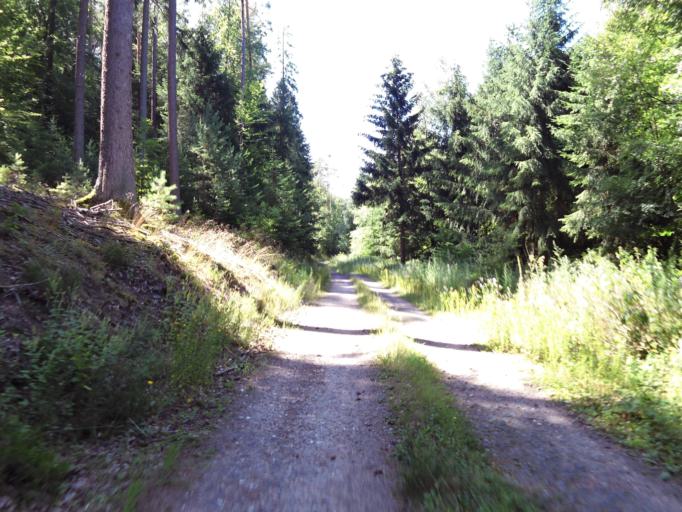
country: DE
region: Rheinland-Pfalz
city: Carlsberg
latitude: 49.4893
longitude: 8.0486
